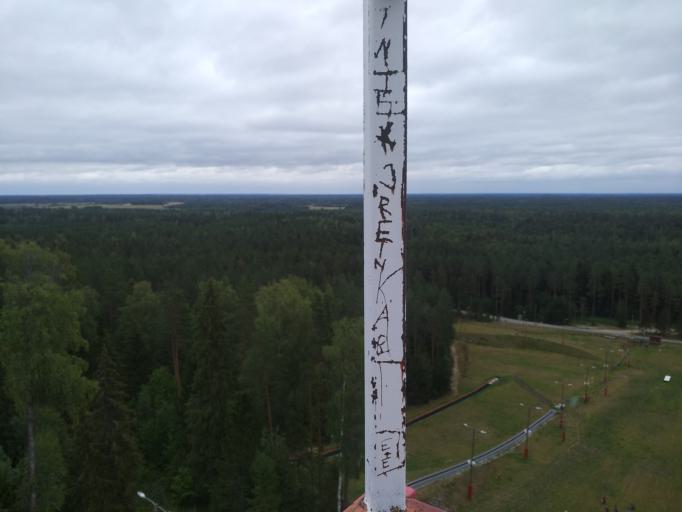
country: EE
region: Harju
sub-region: Kuusalu vald
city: Kuusalu
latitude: 59.2232
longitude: 25.5626
